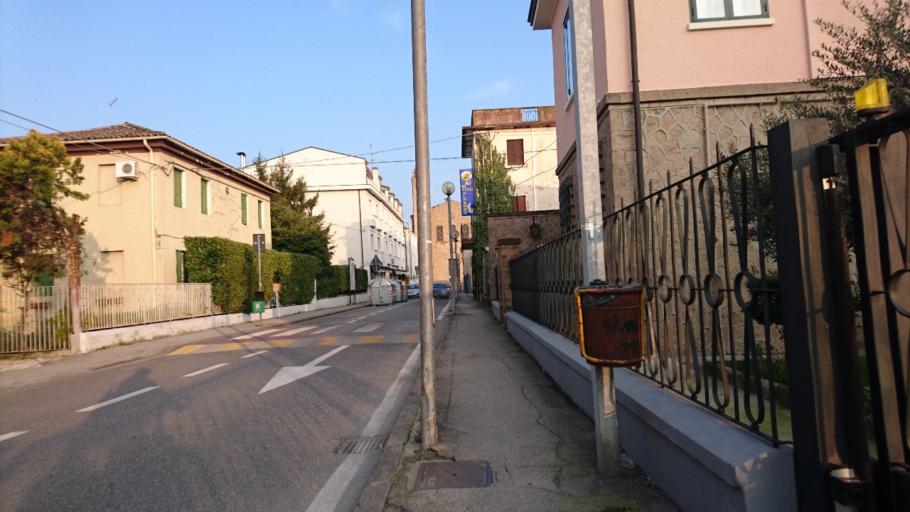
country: IT
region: Veneto
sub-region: Provincia di Padova
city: Abano Terme
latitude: 45.3610
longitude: 11.7886
